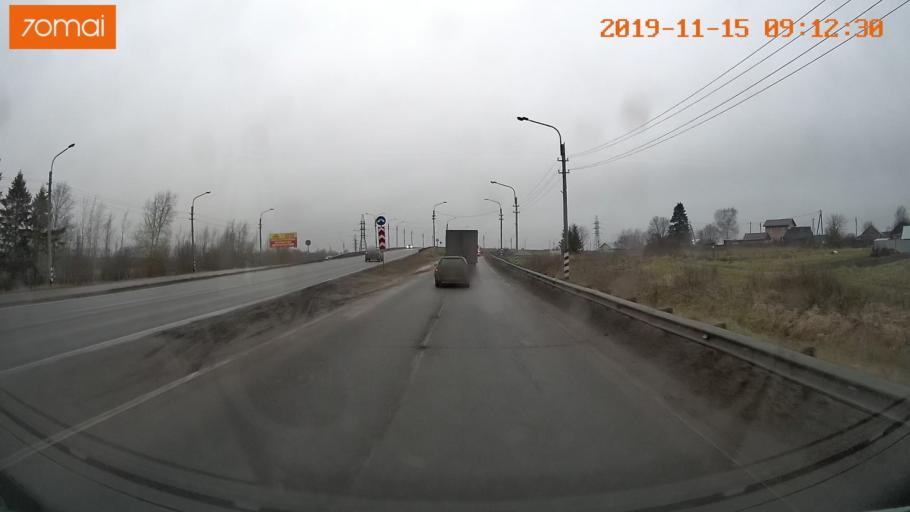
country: RU
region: Vologda
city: Tonshalovo
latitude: 59.2087
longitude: 37.9363
